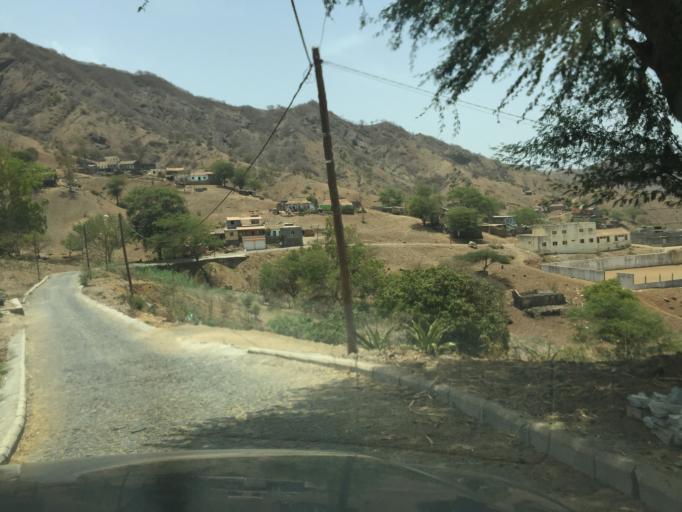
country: CV
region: Sao Salvador do Mundo
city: Picos
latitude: 15.0952
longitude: -23.6477
